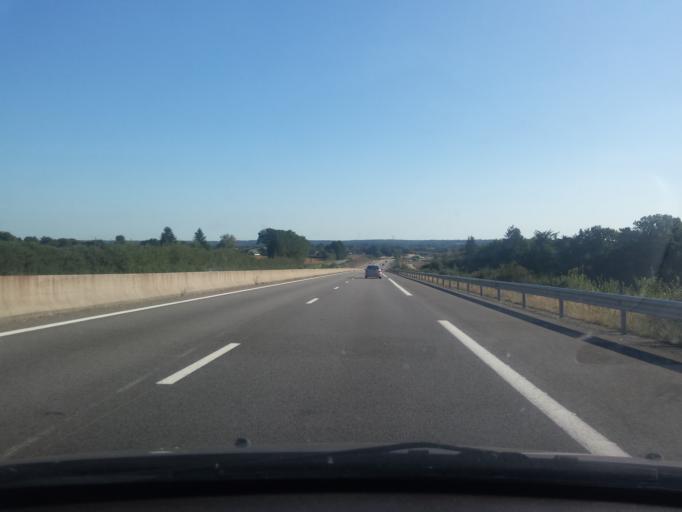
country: FR
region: Brittany
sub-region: Departement du Morbihan
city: Colpo
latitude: 47.7916
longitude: -2.8021
